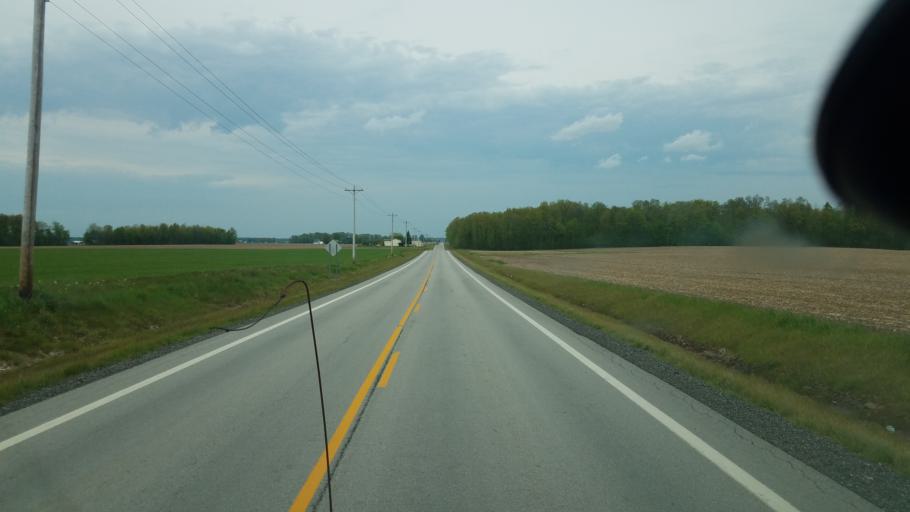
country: US
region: Ohio
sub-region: Huron County
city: Plymouth
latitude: 40.9637
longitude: -82.7433
